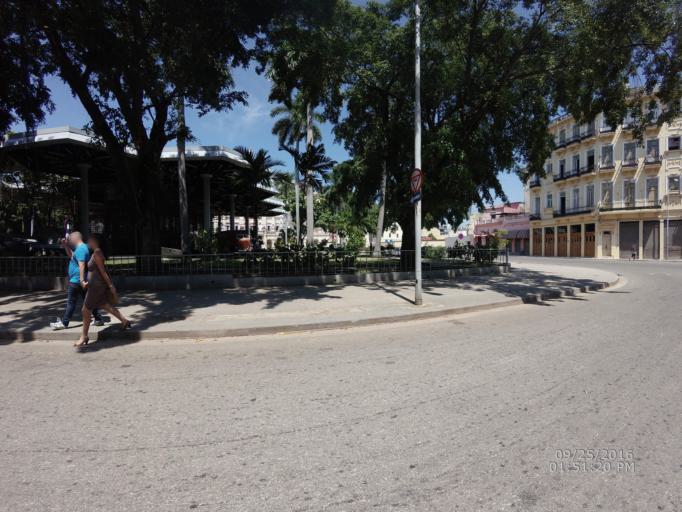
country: CU
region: La Habana
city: Centro Habana
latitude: 23.1406
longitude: -82.3570
